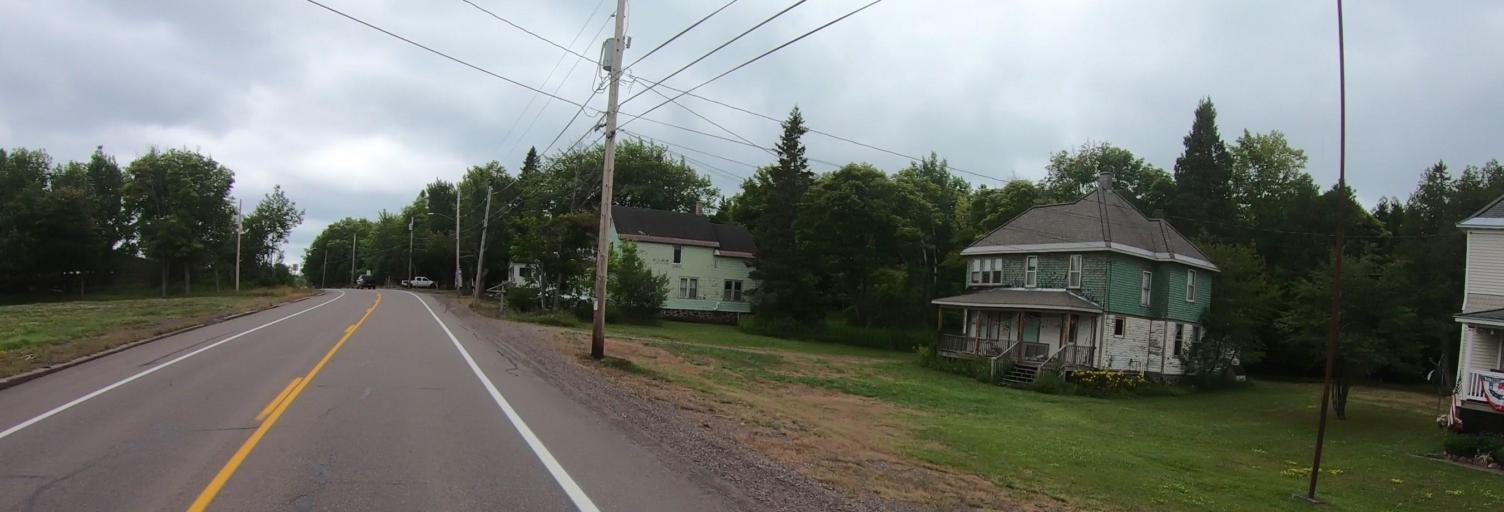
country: US
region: Michigan
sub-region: Houghton County
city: Laurium
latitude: 47.2664
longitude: -88.4234
